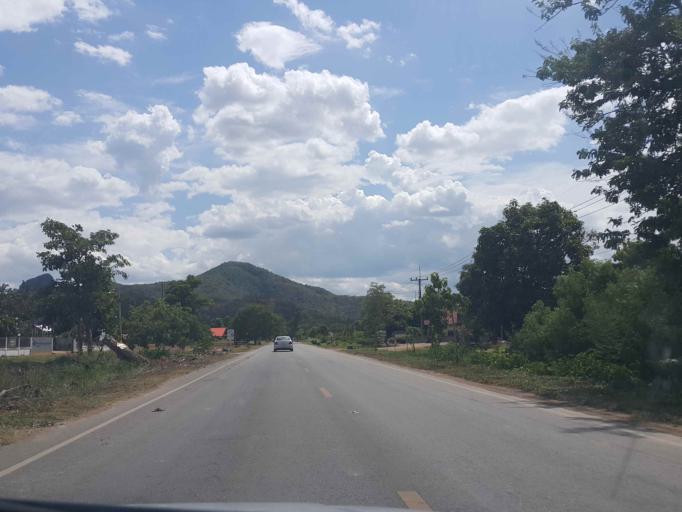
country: TH
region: Sukhothai
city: Thung Saliam
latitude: 17.3285
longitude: 99.5131
